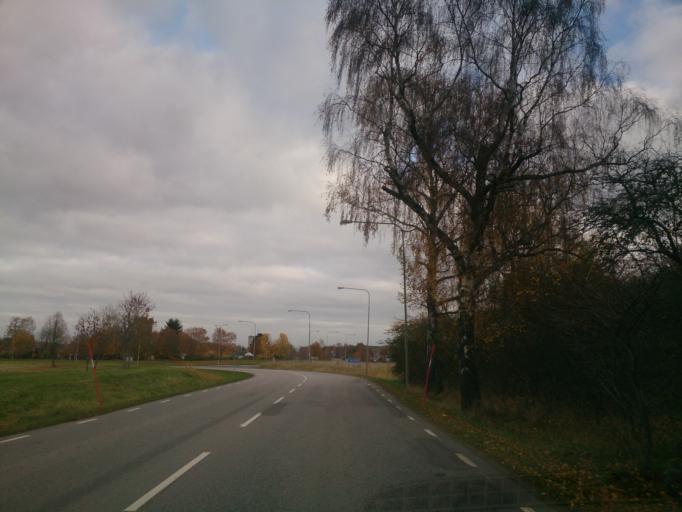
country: SE
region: OEstergoetland
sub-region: Linkopings Kommun
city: Linghem
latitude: 58.4310
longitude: 15.7786
